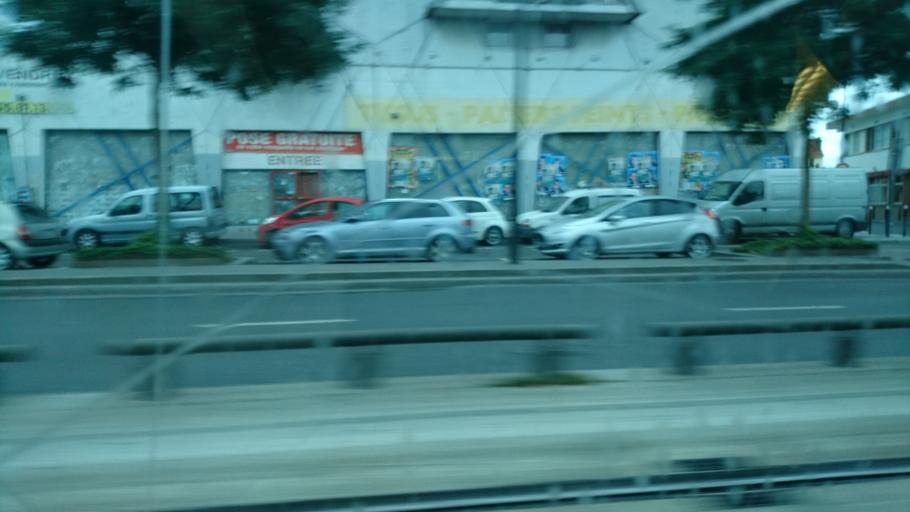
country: FR
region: Ile-de-France
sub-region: Departement de Seine-Saint-Denis
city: Pierrefitte-sur-Seine
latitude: 48.9619
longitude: 2.3590
